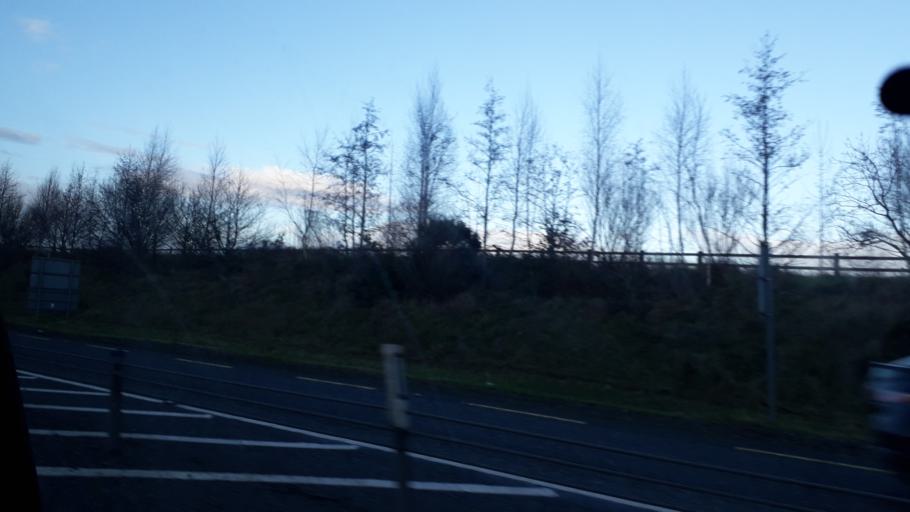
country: IE
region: Ulster
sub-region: County Monaghan
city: Castleblayney
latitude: 54.1169
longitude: -6.7589
